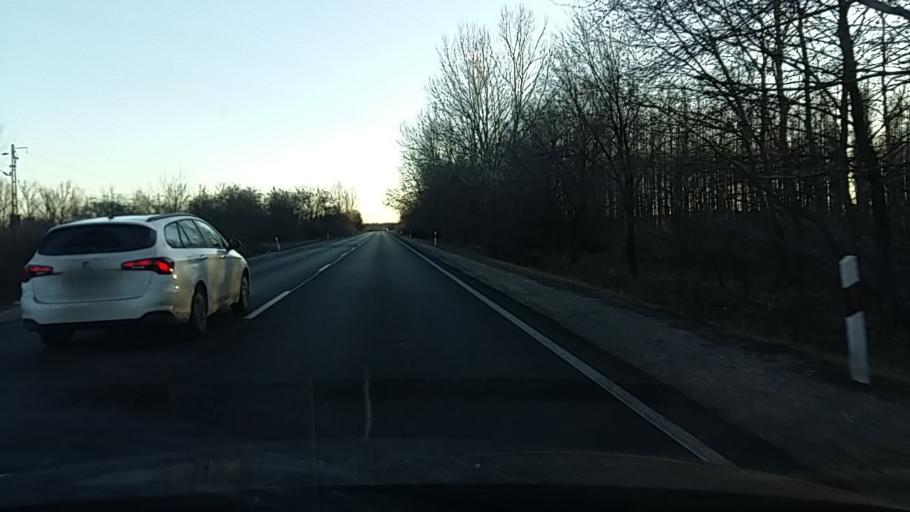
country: HU
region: Szabolcs-Szatmar-Bereg
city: Ujfeherto
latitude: 47.8428
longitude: 21.7045
